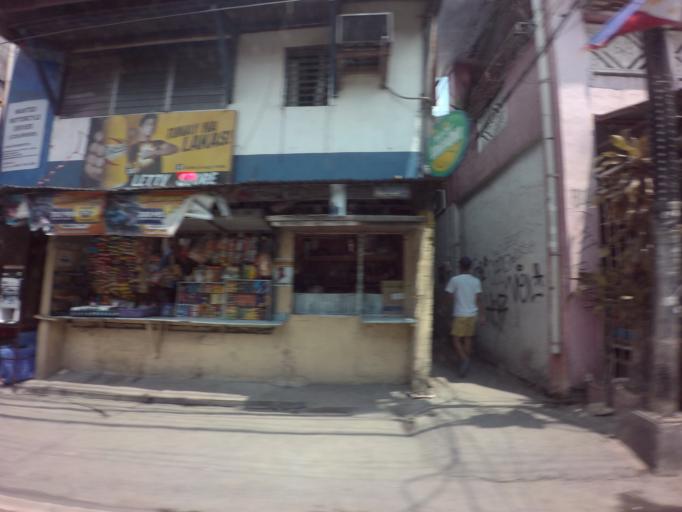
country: PH
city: Sambayanihan People's Village
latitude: 14.4428
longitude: 121.0505
